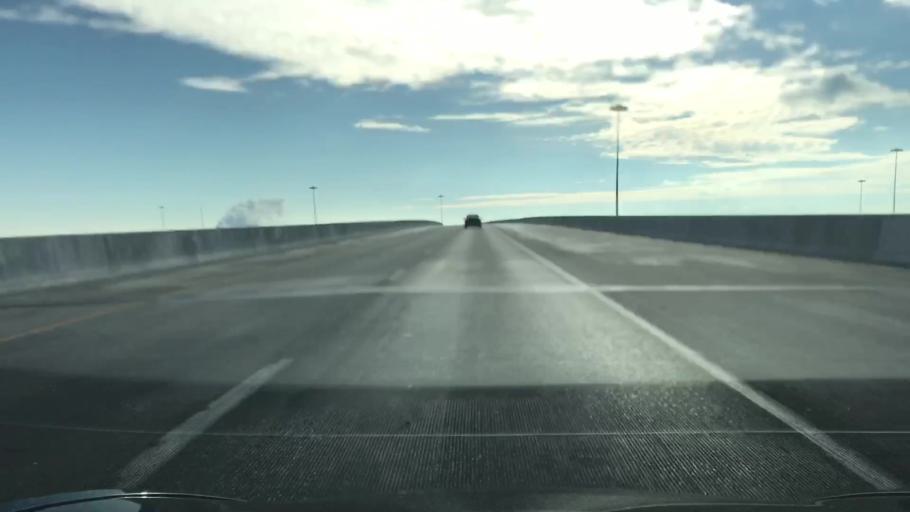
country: US
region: Nebraska
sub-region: Douglas County
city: Omaha
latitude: 41.2361
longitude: -95.9003
